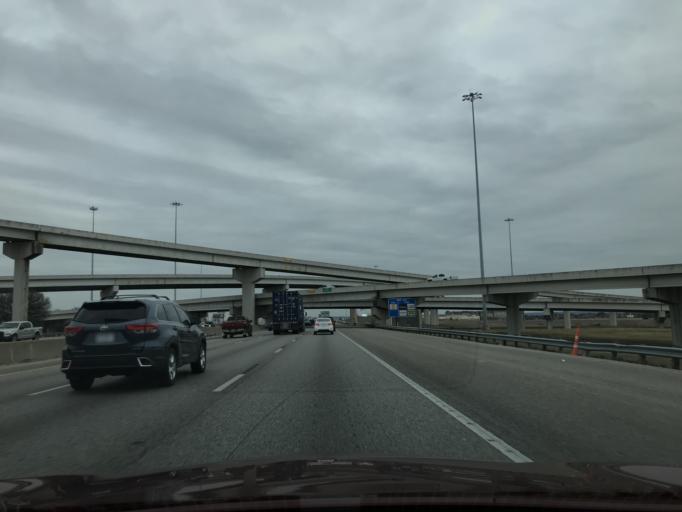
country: US
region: Texas
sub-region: Tarrant County
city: Arlington
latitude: 32.6772
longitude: -97.0645
